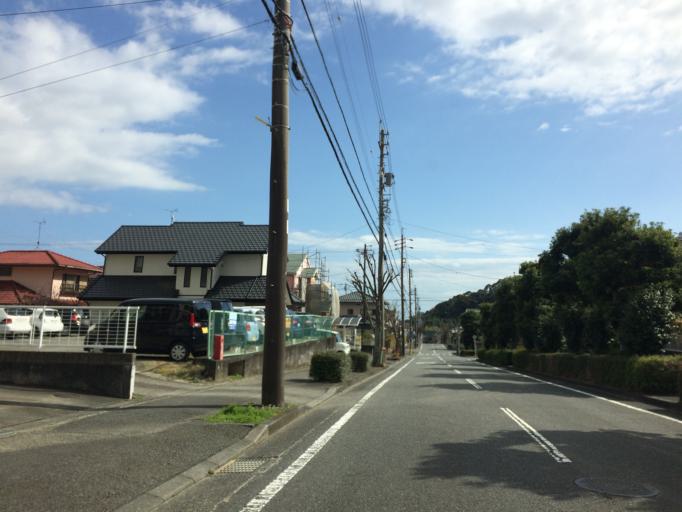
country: JP
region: Shizuoka
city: Fujieda
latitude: 34.8599
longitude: 138.2321
